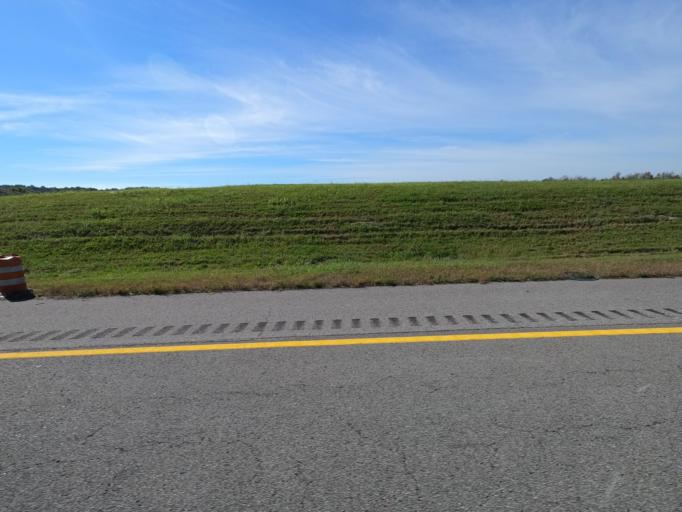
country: US
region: Tennessee
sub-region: Dickson County
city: Burns
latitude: 36.0205
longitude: -87.2599
